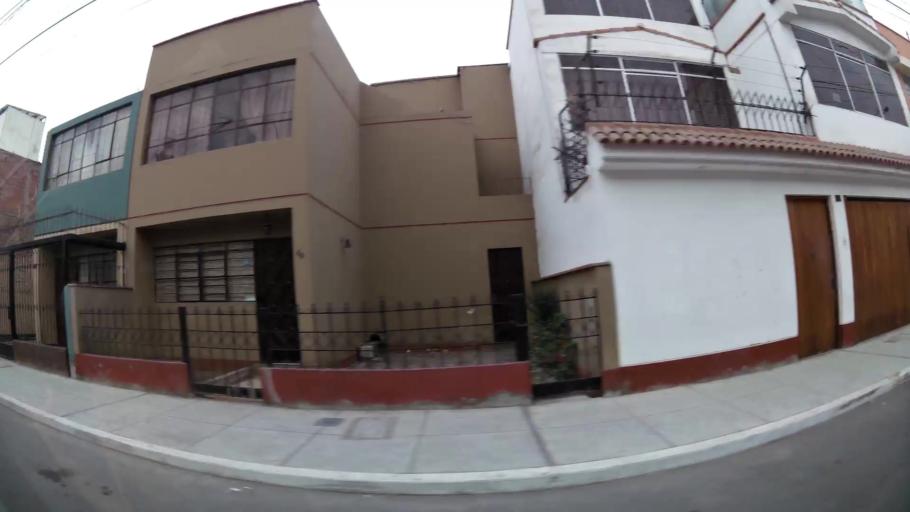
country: PE
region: Lima
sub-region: Lima
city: Surco
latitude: -12.1381
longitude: -77.0202
